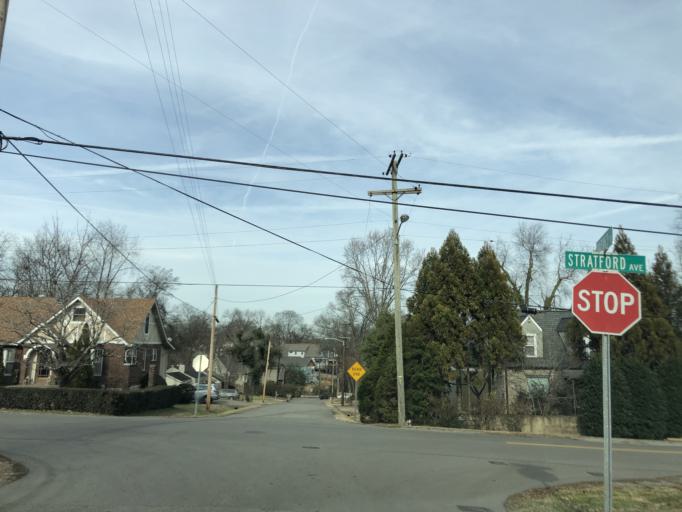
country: US
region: Tennessee
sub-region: Davidson County
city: Nashville
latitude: 36.2140
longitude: -86.7248
